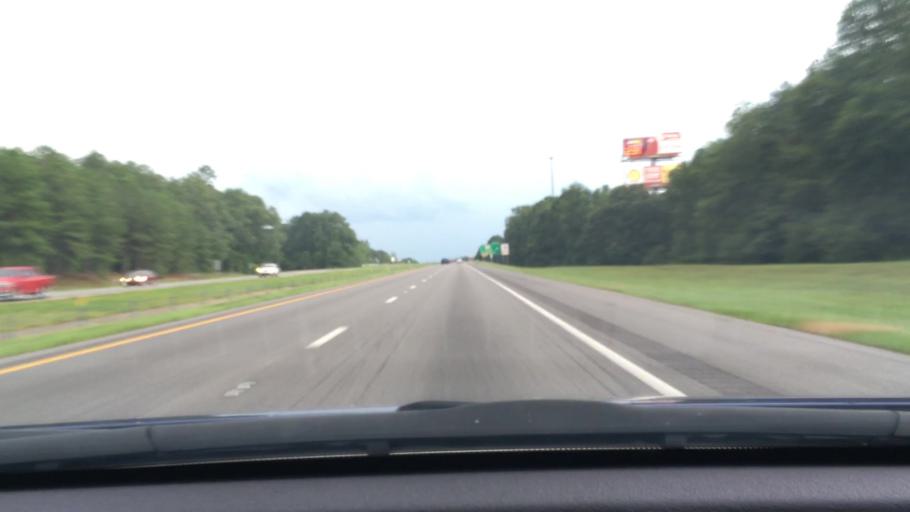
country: US
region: South Carolina
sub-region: Kershaw County
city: Lugoff
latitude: 34.1916
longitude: -80.6817
